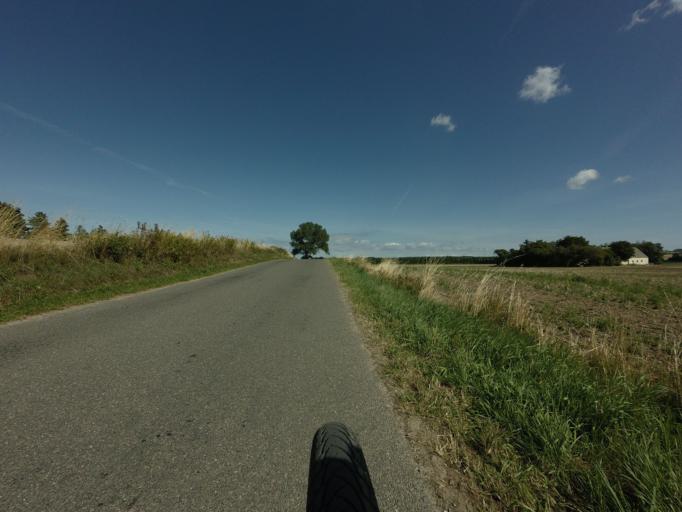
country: DK
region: Zealand
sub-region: Vordingborg Kommune
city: Stege
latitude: 54.9751
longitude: 12.4421
